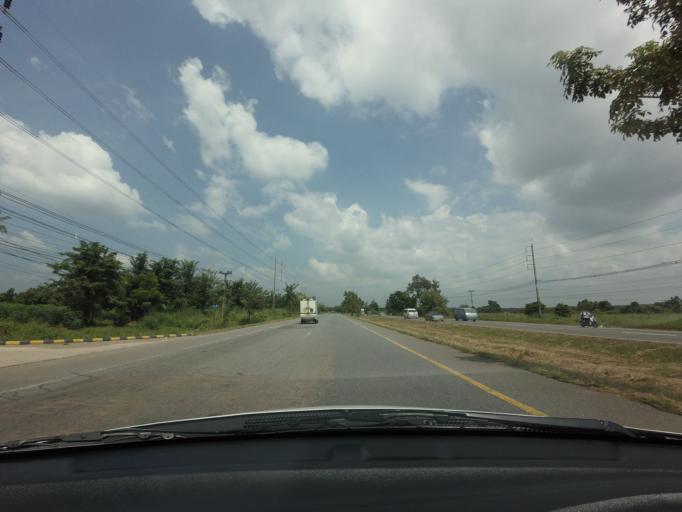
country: TH
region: Prachin Buri
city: Kabin Buri
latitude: 13.9128
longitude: 101.6710
